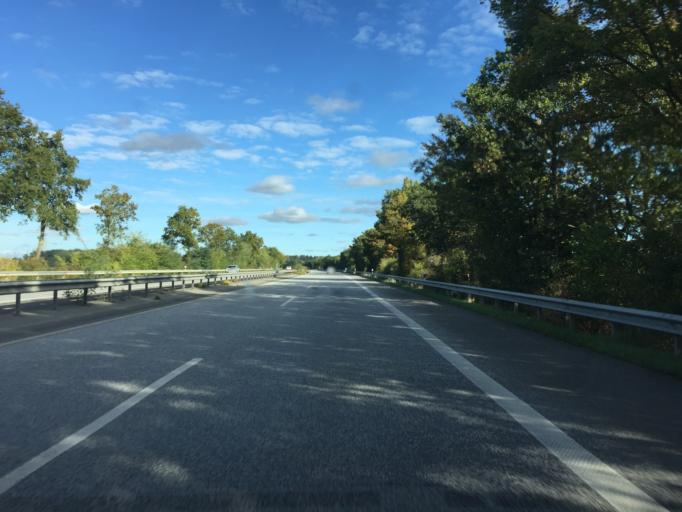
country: DE
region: Schleswig-Holstein
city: Beschendorf
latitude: 54.1756
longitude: 10.8874
